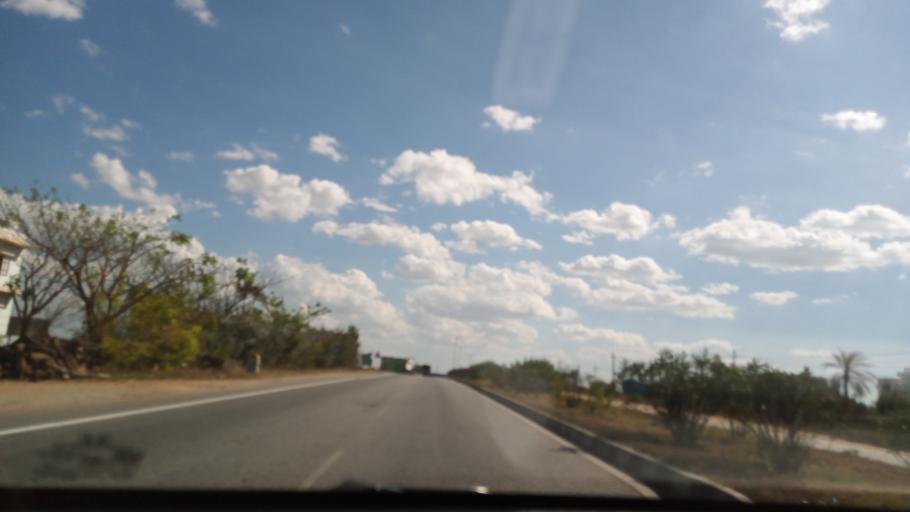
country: IN
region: Karnataka
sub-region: Kolar
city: Mulbagal
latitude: 13.1574
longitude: 78.4048
